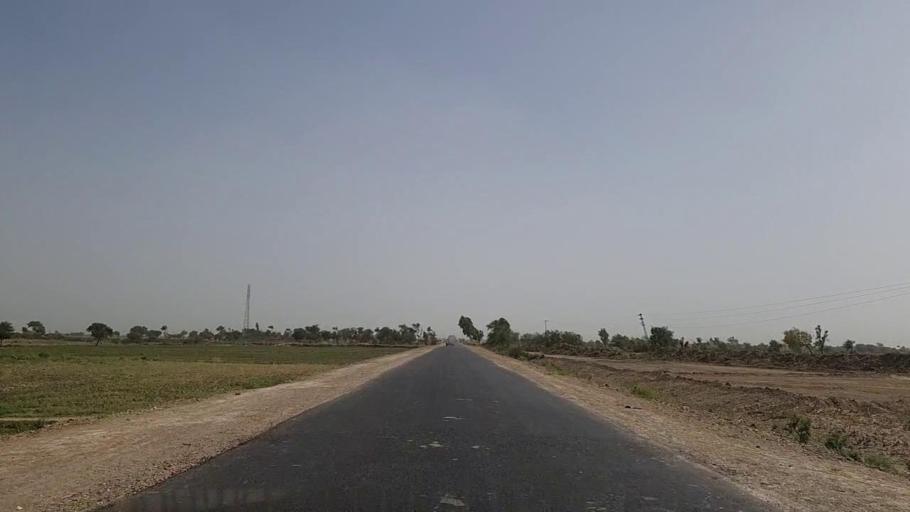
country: PK
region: Sindh
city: Tando Bago
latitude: 24.8296
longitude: 68.8944
